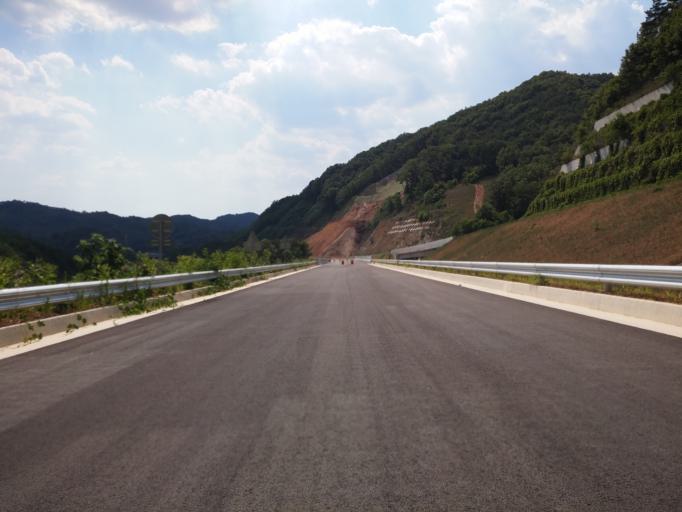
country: KR
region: Daejeon
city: Sintansin
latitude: 36.5046
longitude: 127.4844
